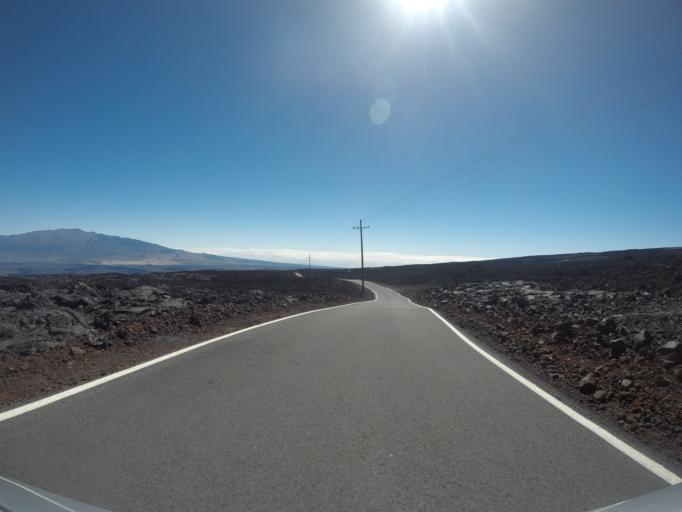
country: US
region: Hawaii
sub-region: Hawaii County
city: Volcano
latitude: 19.5607
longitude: -155.5287
